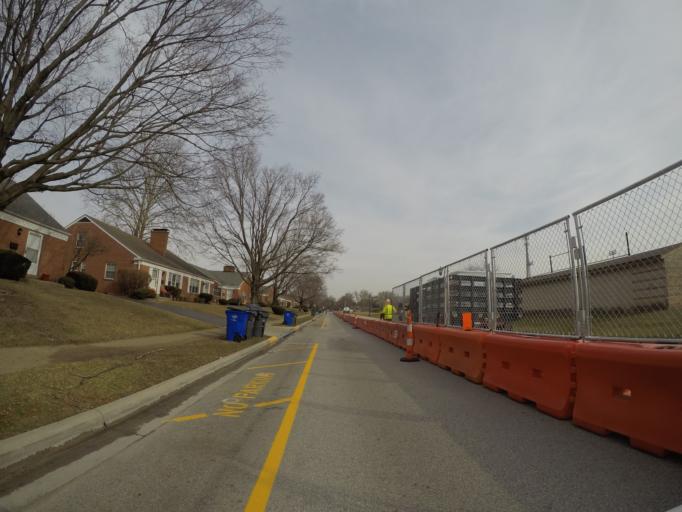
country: US
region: Ohio
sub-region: Franklin County
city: Upper Arlington
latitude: 40.0169
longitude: -83.0563
